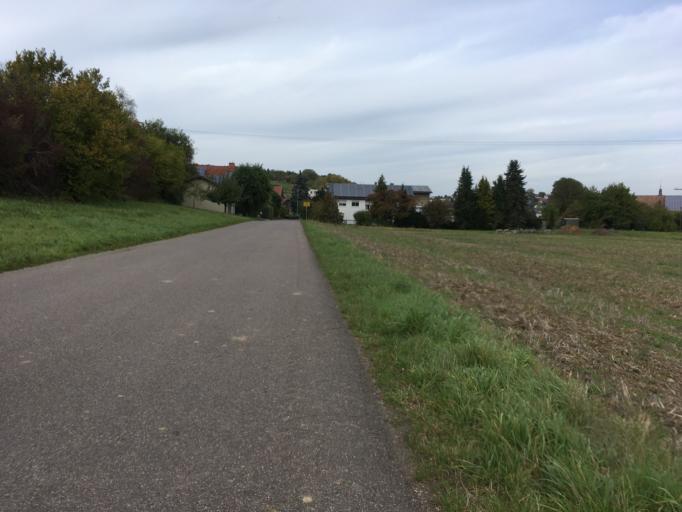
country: DE
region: Baden-Wuerttemberg
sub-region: Karlsruhe Region
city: Rosenberg
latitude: 49.5138
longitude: 9.4384
